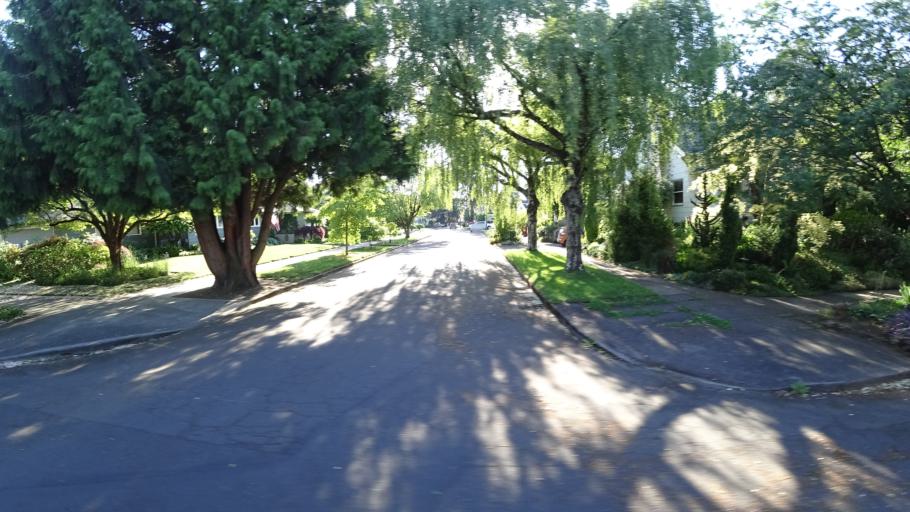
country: US
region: Oregon
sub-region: Multnomah County
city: Portland
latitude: 45.5535
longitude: -122.6872
